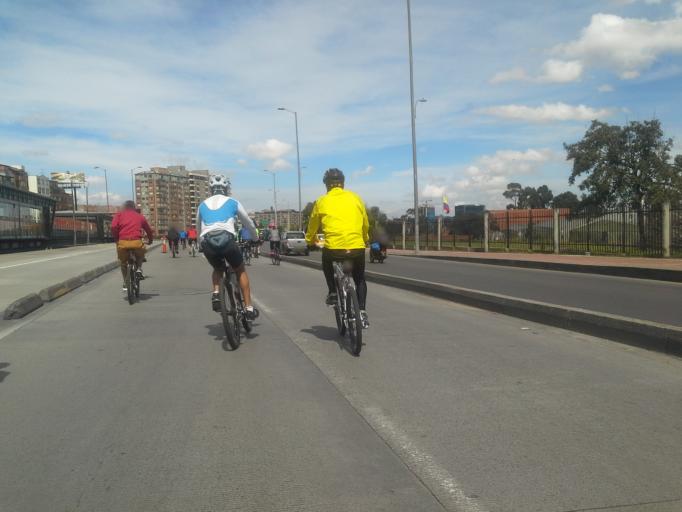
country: CO
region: Bogota D.C.
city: Bogota
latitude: 4.6342
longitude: -74.0892
